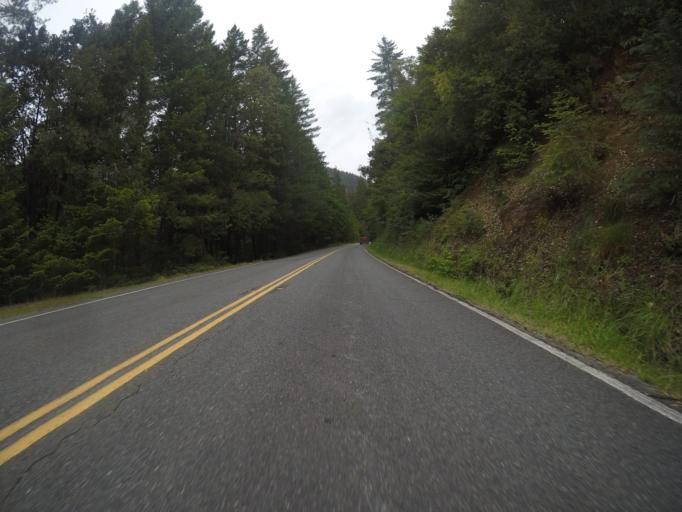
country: US
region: California
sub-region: Del Norte County
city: Bertsch-Oceanview
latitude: 41.7248
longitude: -123.9679
